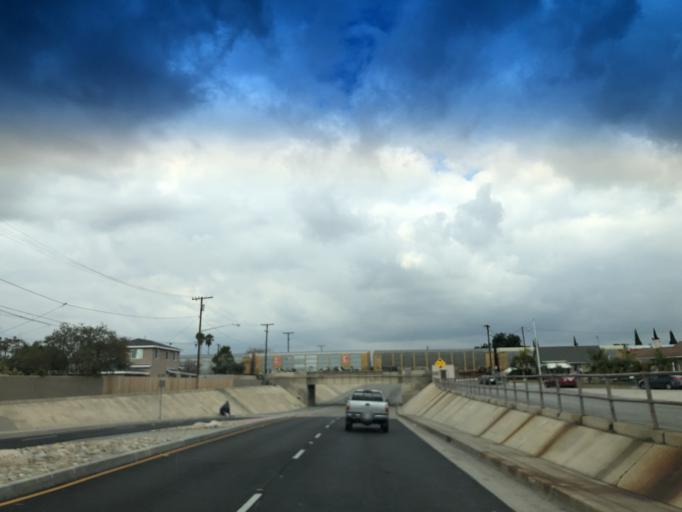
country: US
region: California
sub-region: Los Angeles County
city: Montebello
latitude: 34.0025
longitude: -118.0836
